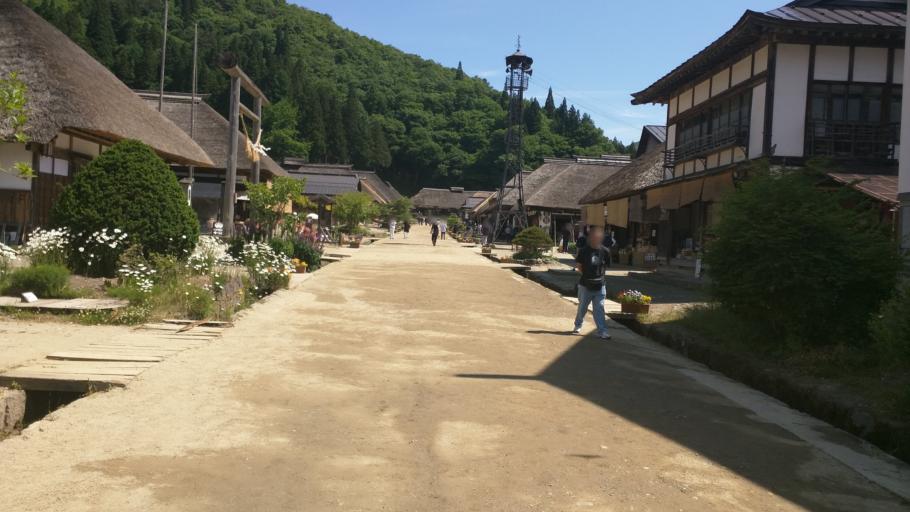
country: JP
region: Fukushima
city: Kitakata
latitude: 37.3335
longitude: 139.8607
